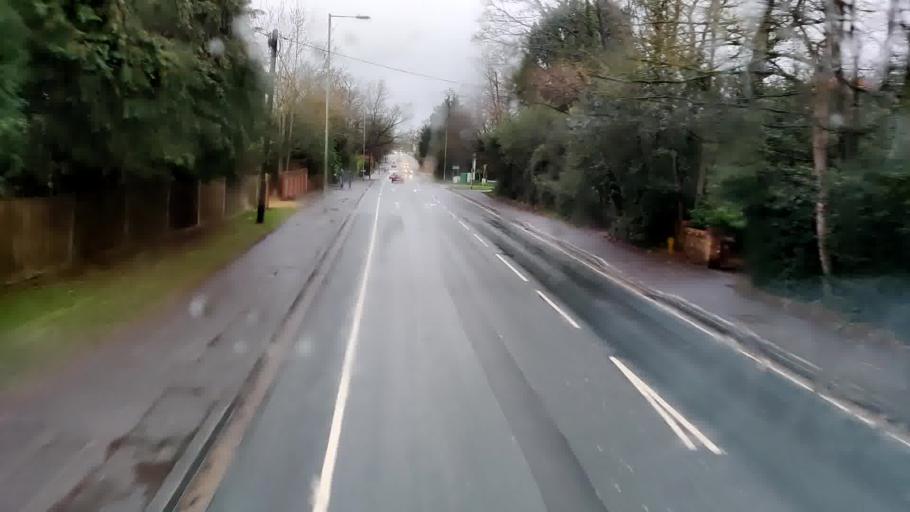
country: GB
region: England
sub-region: Wokingham
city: Winnersh
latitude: 51.4224
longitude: -0.8629
